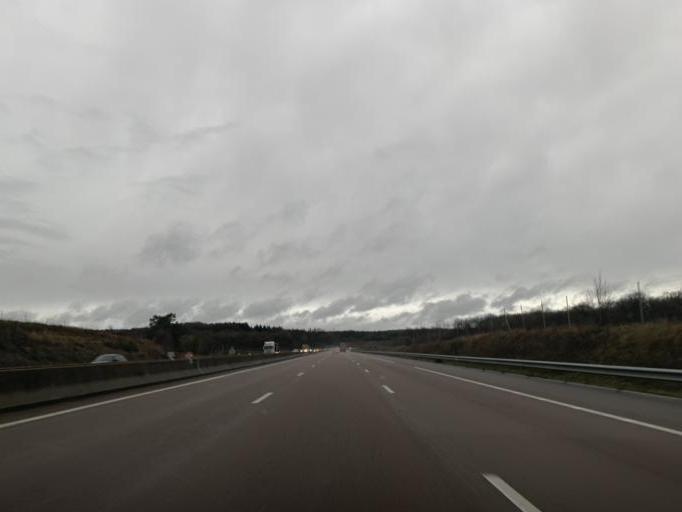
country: FR
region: Bourgogne
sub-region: Departement de la Cote-d'Or
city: Selongey
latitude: 47.7539
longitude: 5.1912
